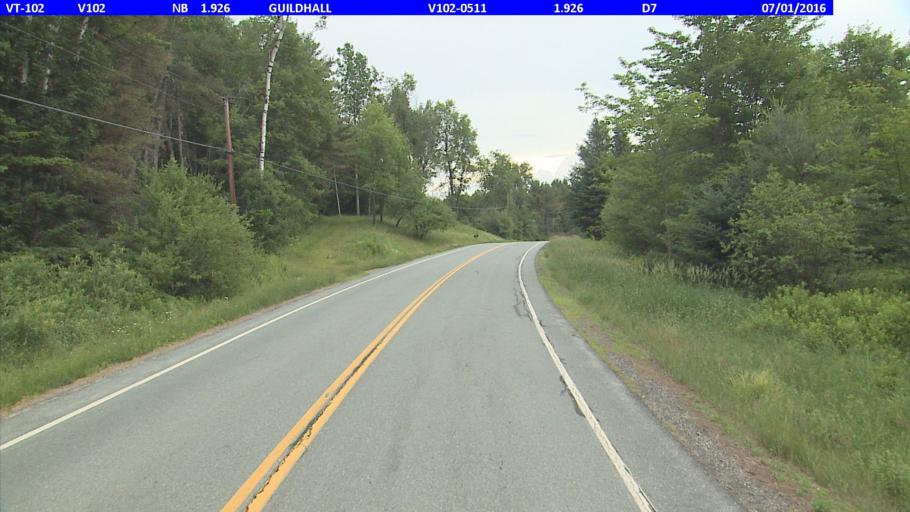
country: US
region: New Hampshire
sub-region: Coos County
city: Lancaster
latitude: 44.5230
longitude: -71.5951
